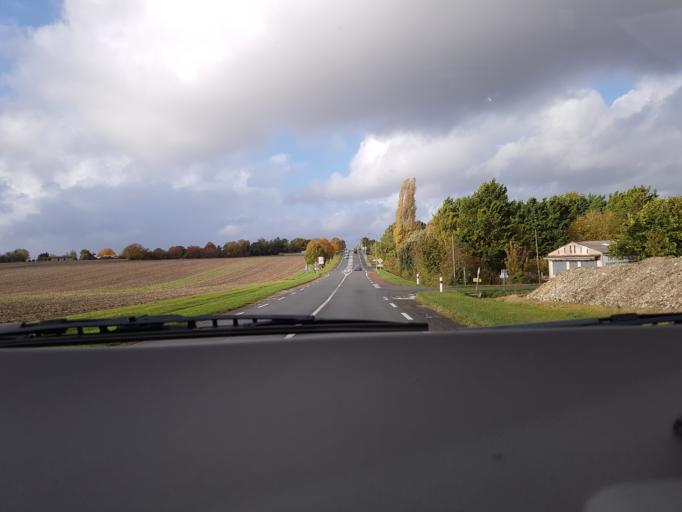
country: FR
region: Poitou-Charentes
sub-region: Departement de la Charente-Maritime
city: Thenac
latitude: 45.6489
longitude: -0.5849
